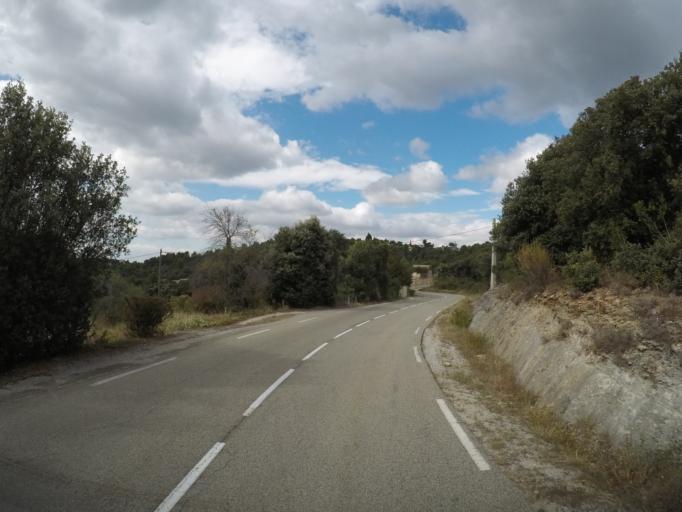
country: FR
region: Rhone-Alpes
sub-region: Departement de la Drome
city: Buis-les-Baronnies
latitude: 44.2274
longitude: 5.1998
